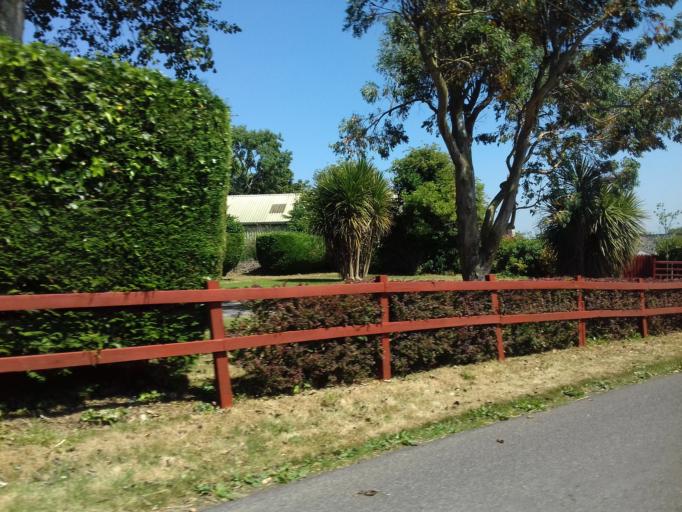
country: IE
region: Leinster
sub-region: An Mhi
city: Ashbourne
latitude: 53.5284
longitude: -6.3238
